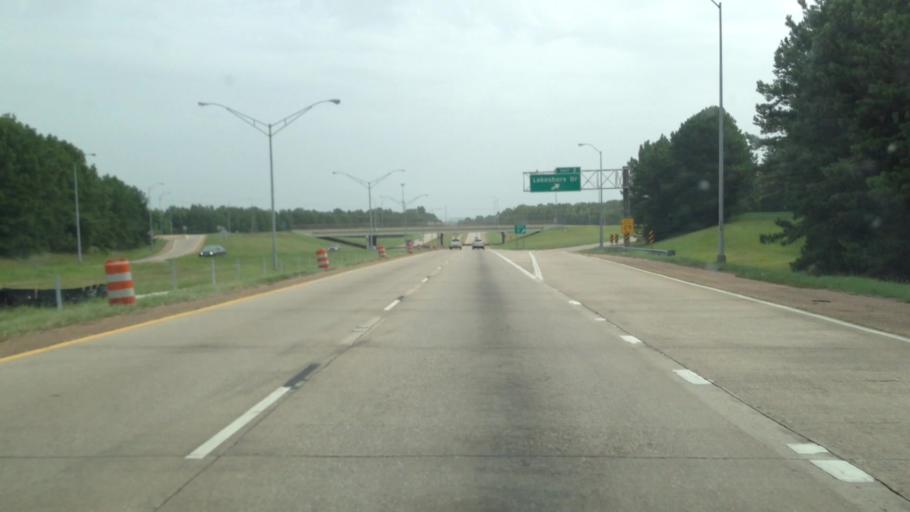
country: US
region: Louisiana
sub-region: Caddo Parish
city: Shreveport
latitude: 32.4824
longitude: -93.8304
